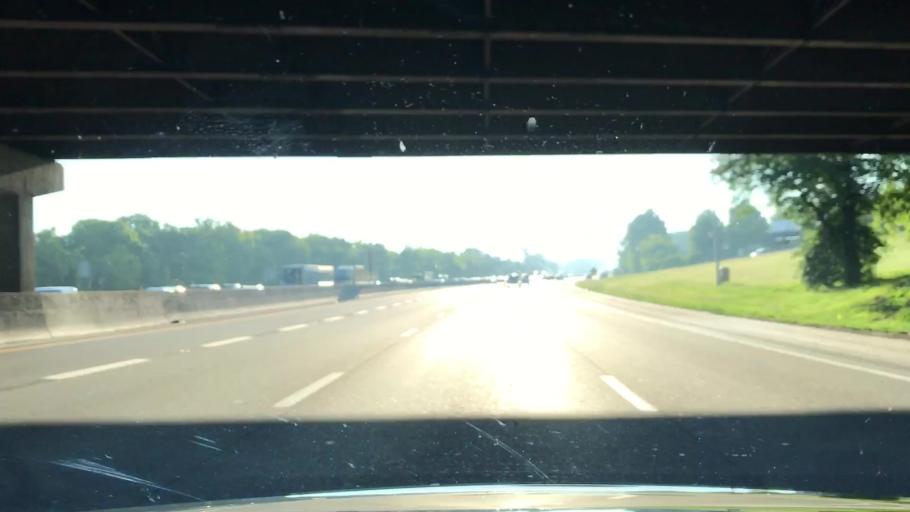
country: US
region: Tennessee
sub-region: Wilson County
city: Green Hill
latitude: 36.1699
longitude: -86.6004
